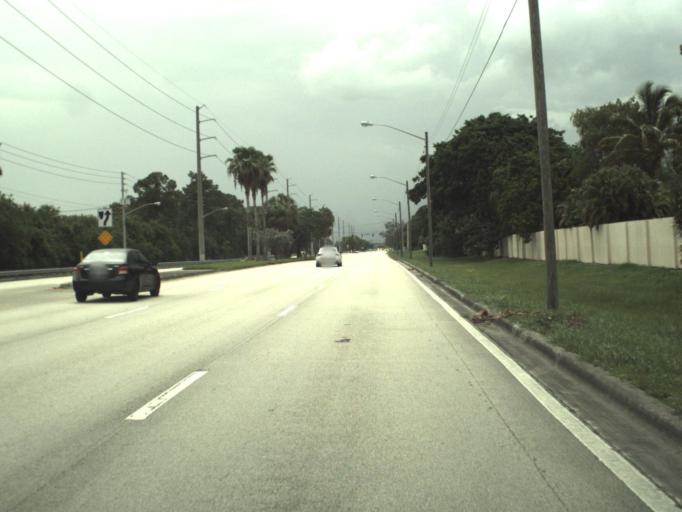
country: US
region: Florida
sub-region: Palm Beach County
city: Boca Pointe
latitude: 26.3496
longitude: -80.1916
